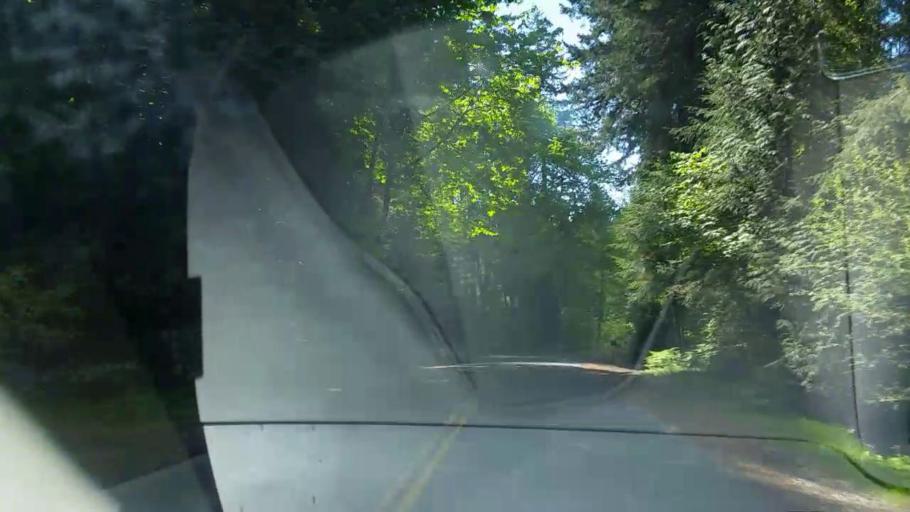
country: US
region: Washington
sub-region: Pierce County
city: Key Center
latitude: 47.3373
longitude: -122.7658
